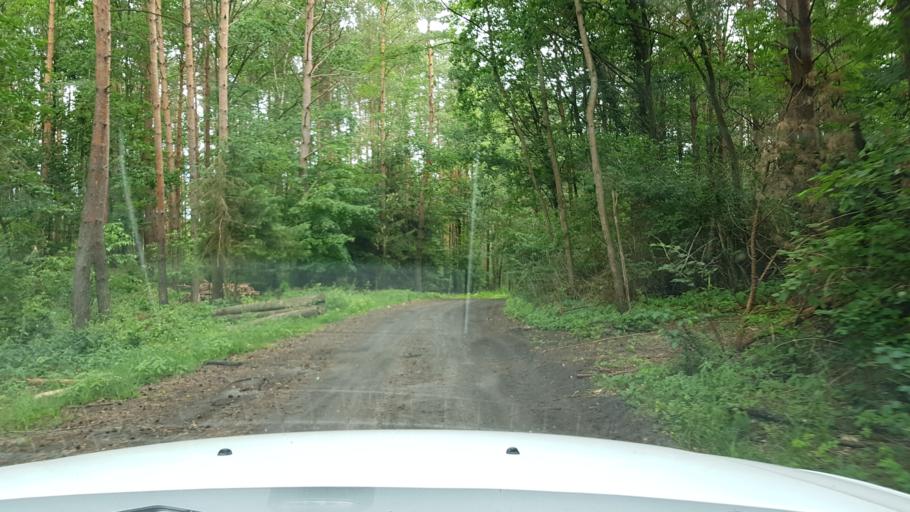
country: PL
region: West Pomeranian Voivodeship
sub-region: Powiat mysliborski
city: Boleszkowice
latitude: 52.6736
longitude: 14.5925
